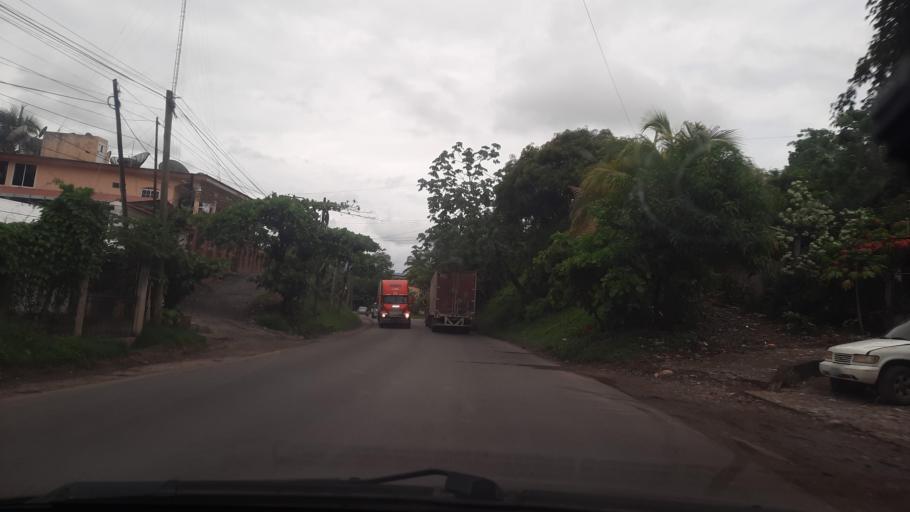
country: GT
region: Izabal
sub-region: Municipio de Los Amates
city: Los Amates
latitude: 15.2753
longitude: -89.0791
